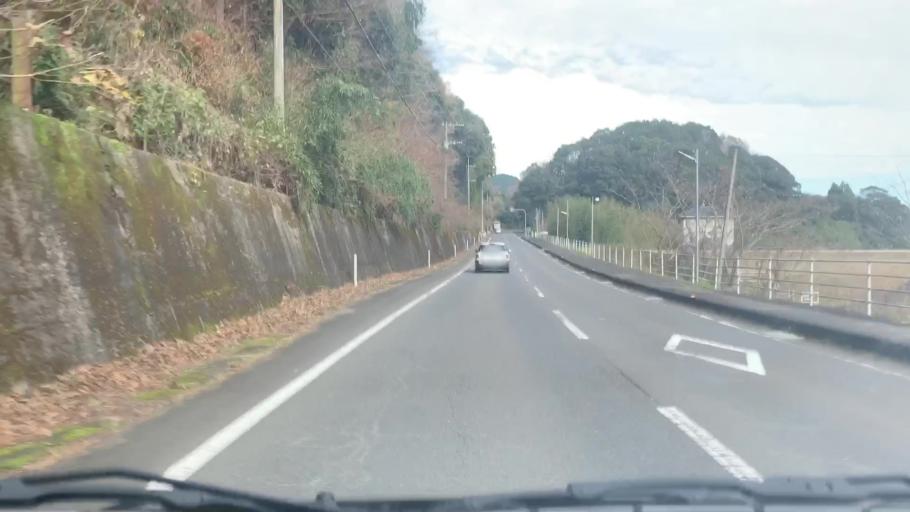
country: JP
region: Saga Prefecture
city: Imaricho-ko
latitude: 33.3172
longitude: 129.9695
